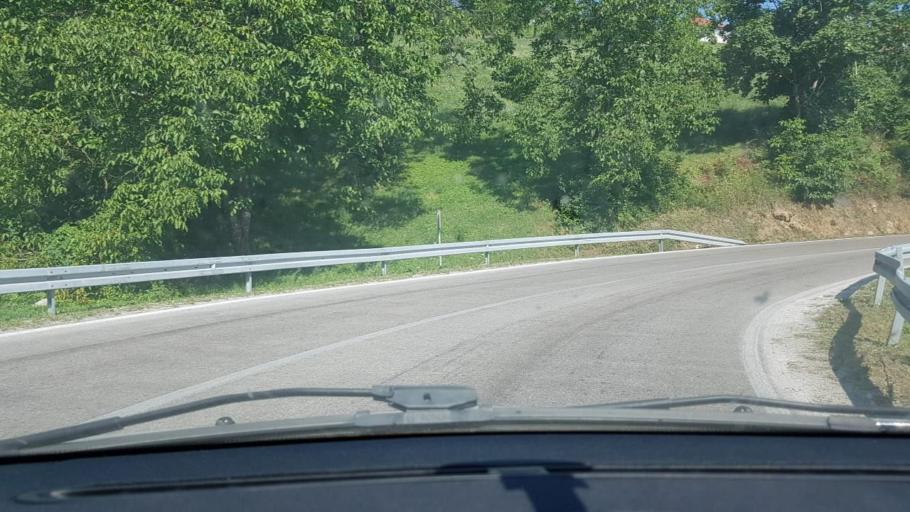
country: BA
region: Federation of Bosnia and Herzegovina
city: Pecigrad
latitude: 45.0449
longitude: 15.9071
